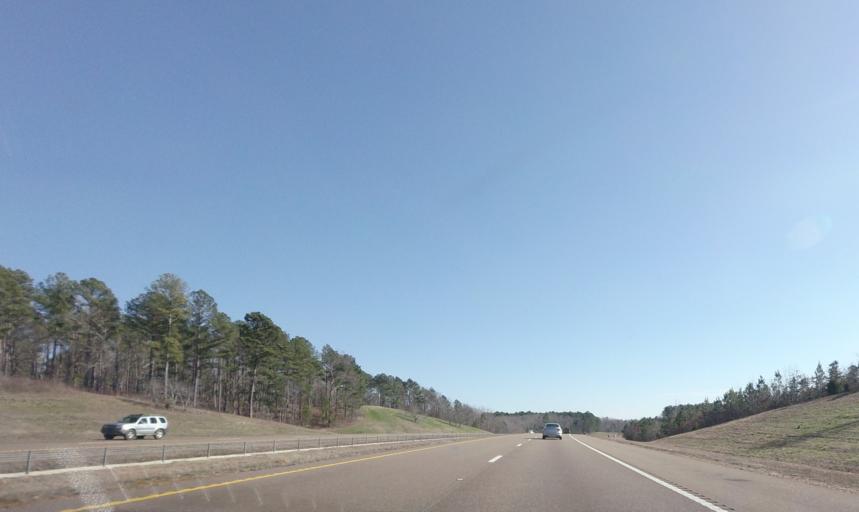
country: US
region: Mississippi
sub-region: Benton County
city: Ashland
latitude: 34.6311
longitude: -89.2147
